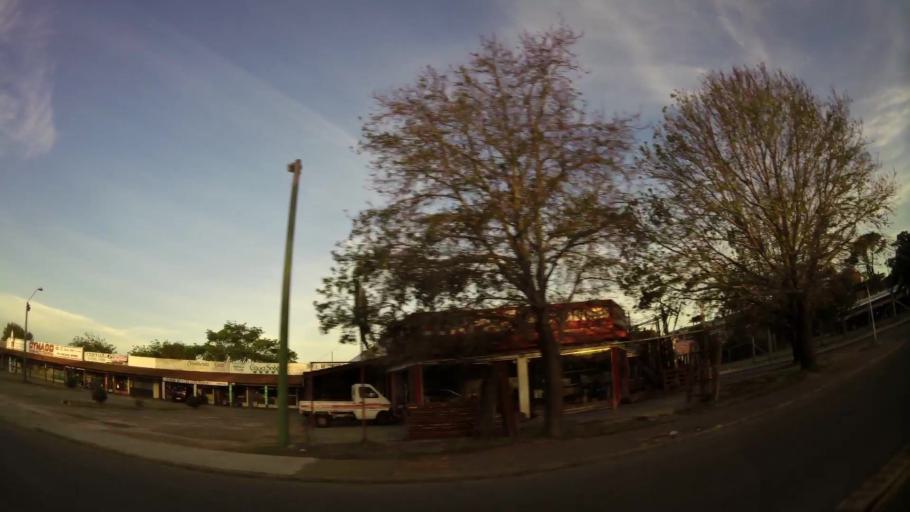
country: UY
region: Maldonado
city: Maldonado
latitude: -34.9142
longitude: -54.9531
